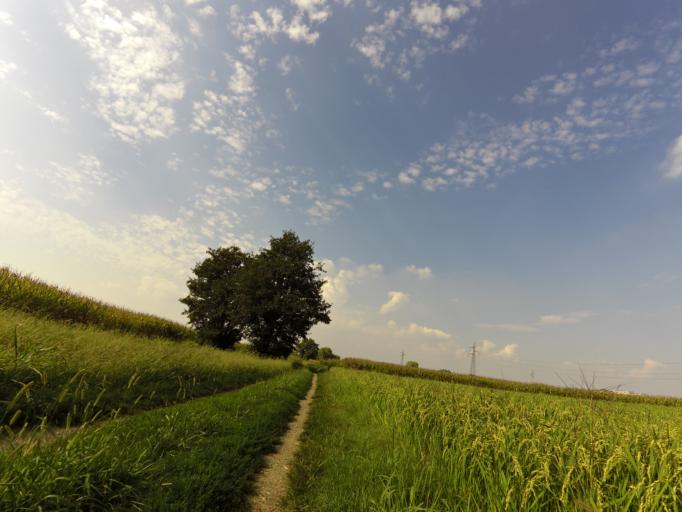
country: IT
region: Lombardy
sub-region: Citta metropolitana di Milano
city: Civesio
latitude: 45.3902
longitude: 9.2741
